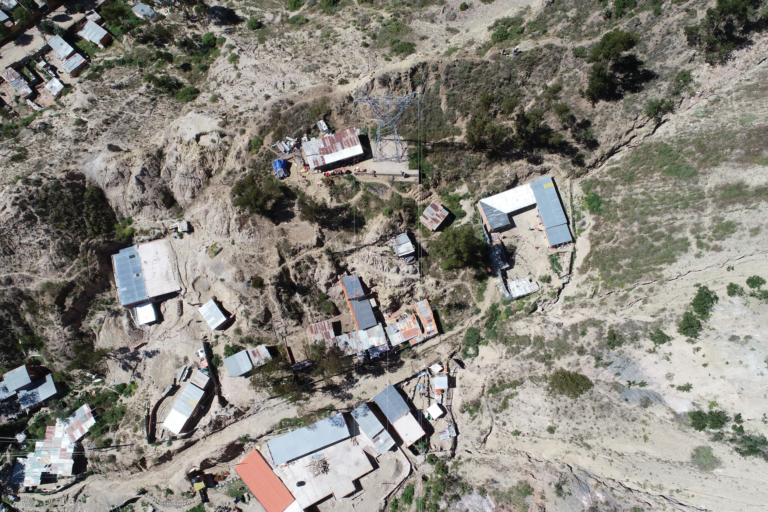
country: BO
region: La Paz
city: La Paz
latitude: -16.5269
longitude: -68.0917
